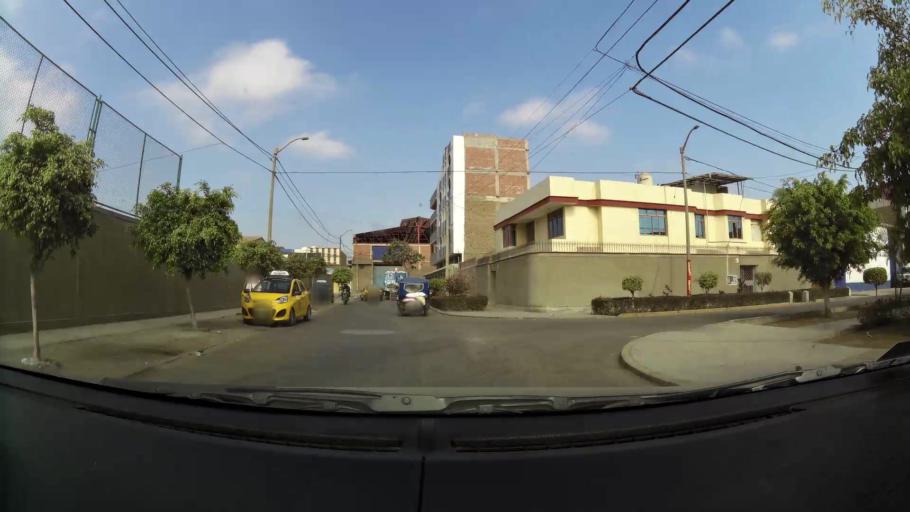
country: PE
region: La Libertad
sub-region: Provincia de Trujillo
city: Trujillo
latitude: -8.1126
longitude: -79.0155
